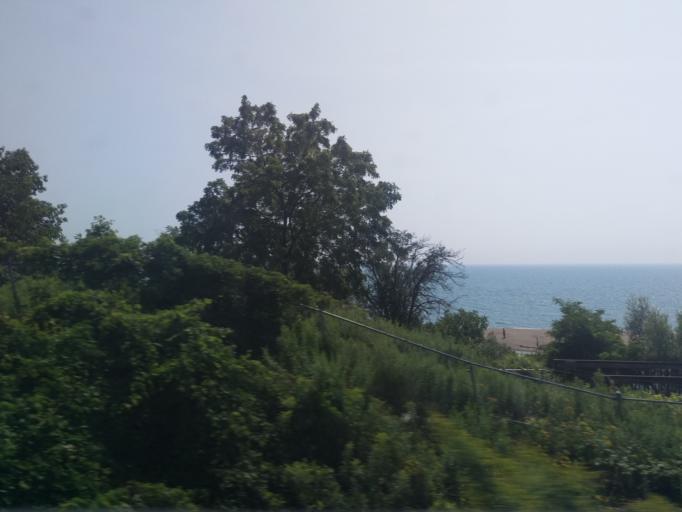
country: CA
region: Ontario
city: Ajax
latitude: 43.7949
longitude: -79.1178
